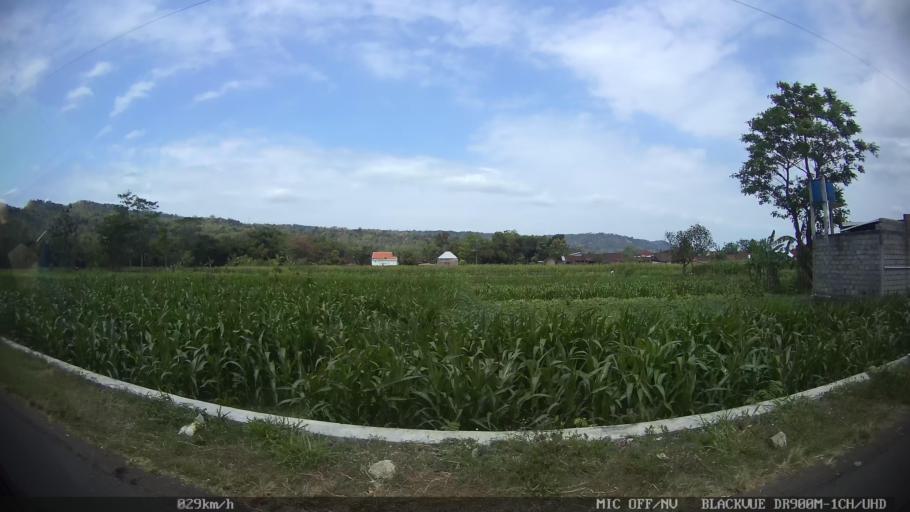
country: ID
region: Central Java
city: Candi Prambanan
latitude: -7.8115
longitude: 110.5015
